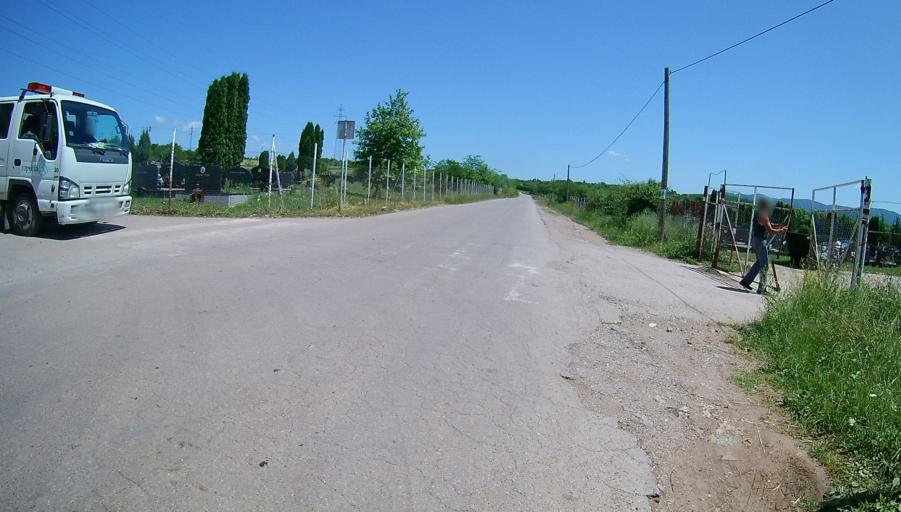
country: RS
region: Central Serbia
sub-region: Nisavski Okrug
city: Nis
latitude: 43.2963
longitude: 21.8851
